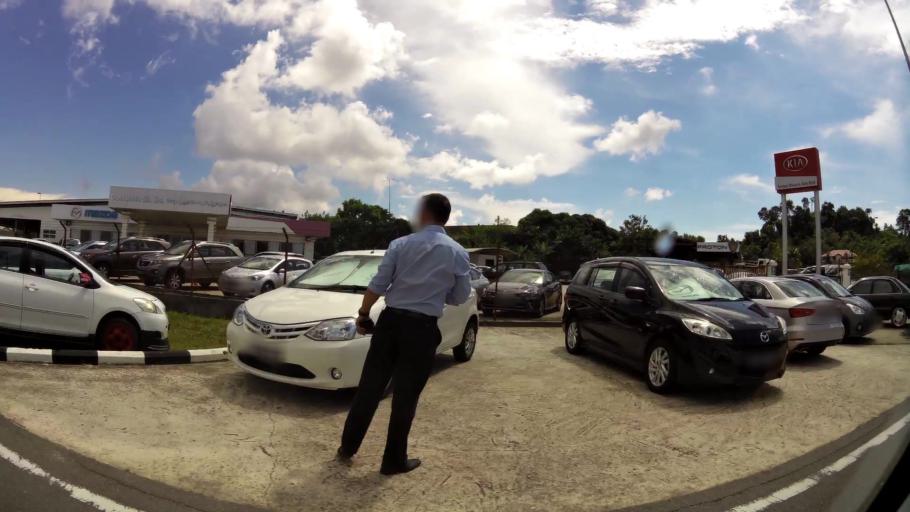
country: BN
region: Brunei and Muara
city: Bandar Seri Begawan
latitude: 4.9825
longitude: 114.9540
